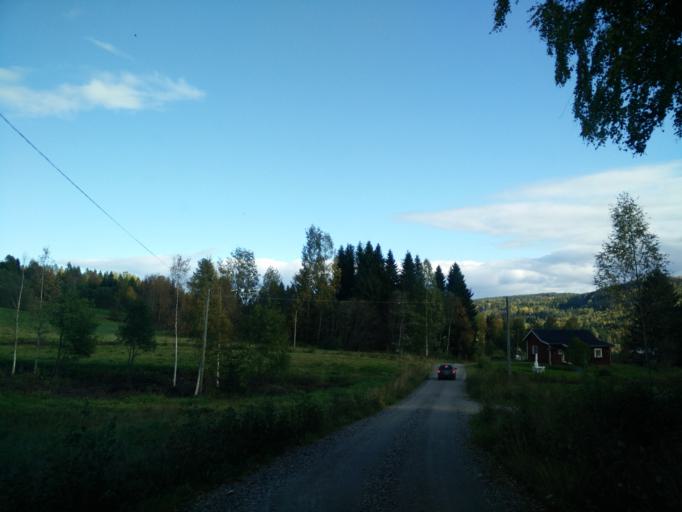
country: SE
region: Vaesternorrland
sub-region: Sundsvalls Kommun
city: Matfors
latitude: 62.3334
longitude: 16.9379
